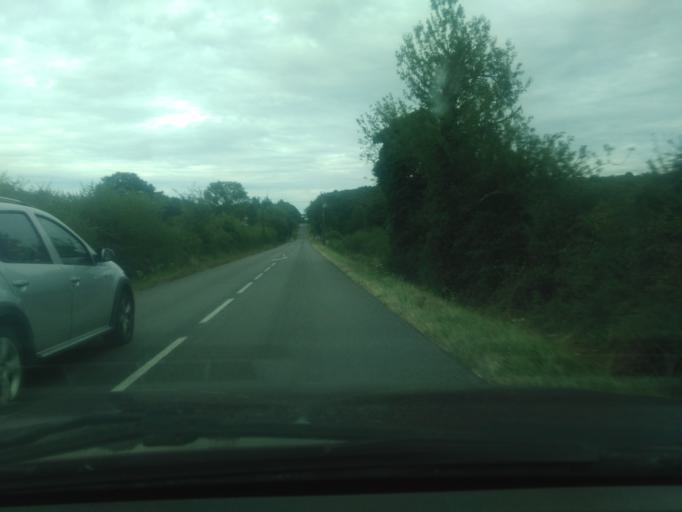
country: FR
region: Bourgogne
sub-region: Departement de la Nievre
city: Dornes
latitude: 46.7710
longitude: 3.3202
